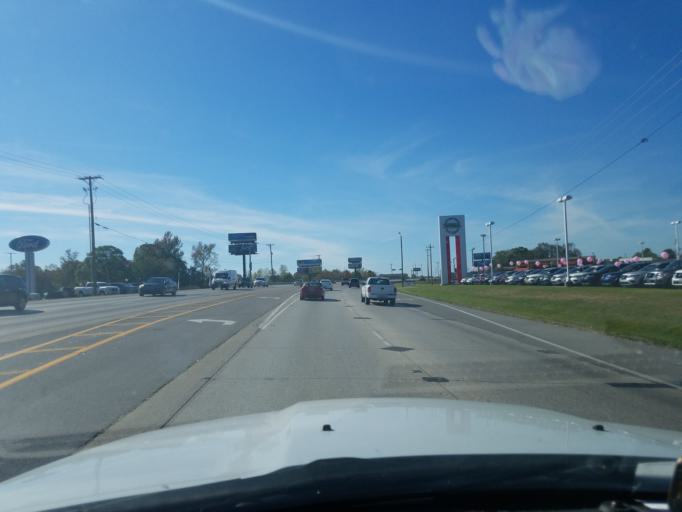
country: US
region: Kentucky
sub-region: Laurel County
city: London
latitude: 37.1052
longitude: -84.0784
